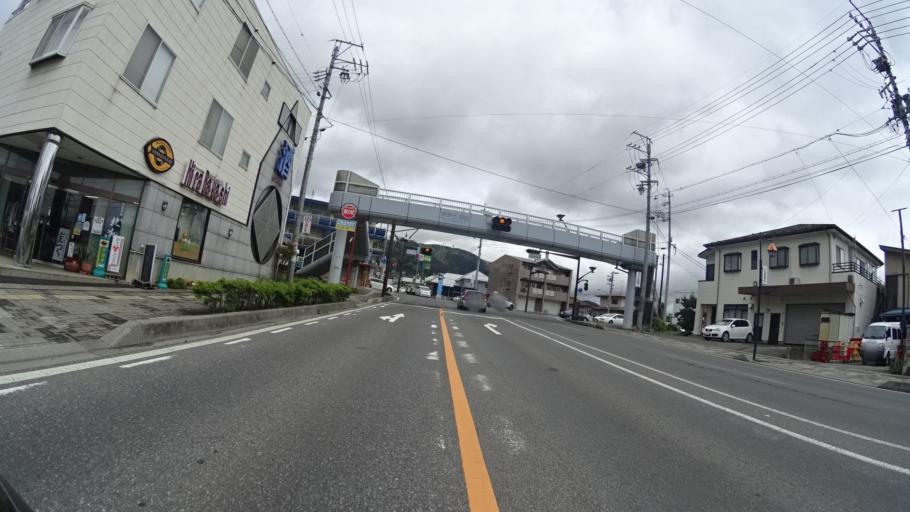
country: JP
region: Nagano
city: Nagano-shi
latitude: 36.6755
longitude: 138.1998
